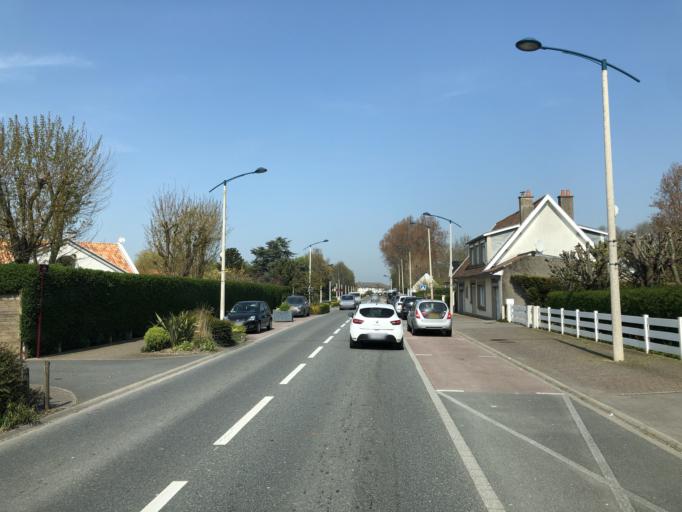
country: FR
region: Nord-Pas-de-Calais
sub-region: Departement du Pas-de-Calais
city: Coquelles
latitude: 50.9381
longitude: 1.8015
